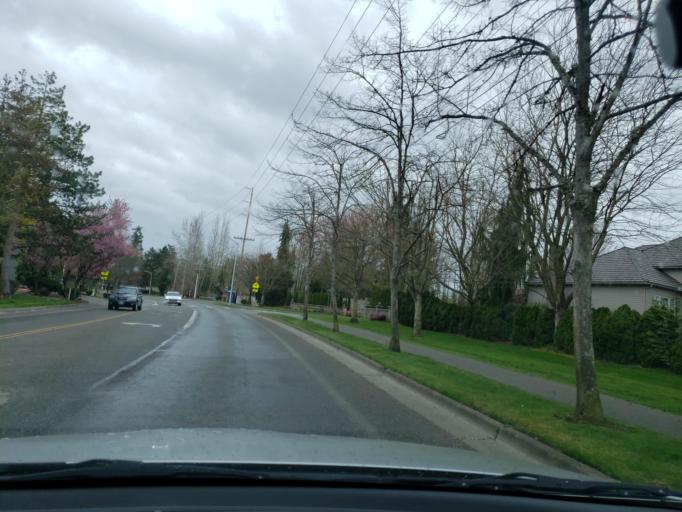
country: US
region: Washington
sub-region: Snohomish County
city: Meadowdale
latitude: 47.8882
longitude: -122.3108
